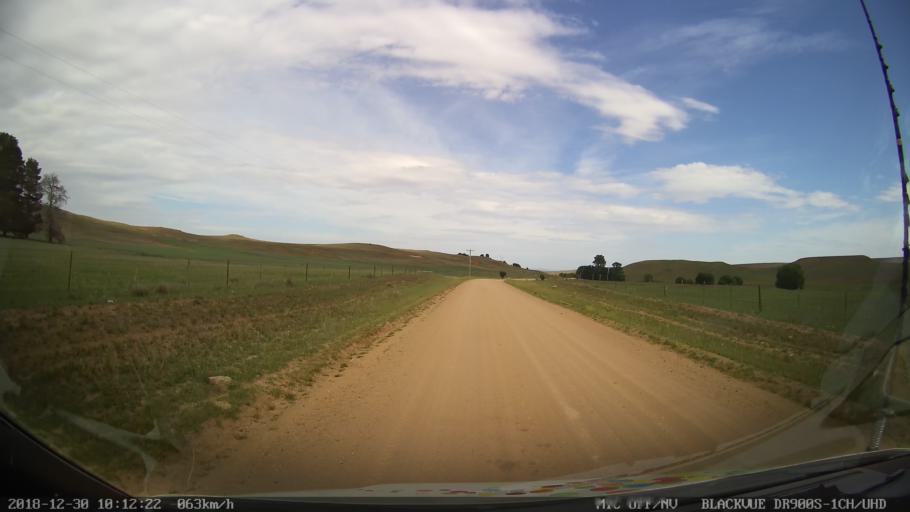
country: AU
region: New South Wales
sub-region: Snowy River
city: Berridale
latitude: -36.5421
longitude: 149.0764
